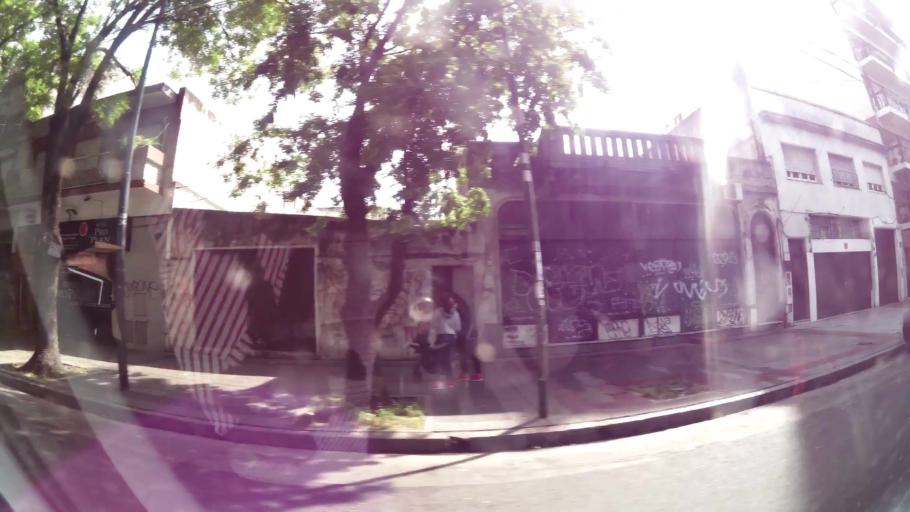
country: AR
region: Buenos Aires F.D.
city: Buenos Aires
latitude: -34.6436
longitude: -58.4224
